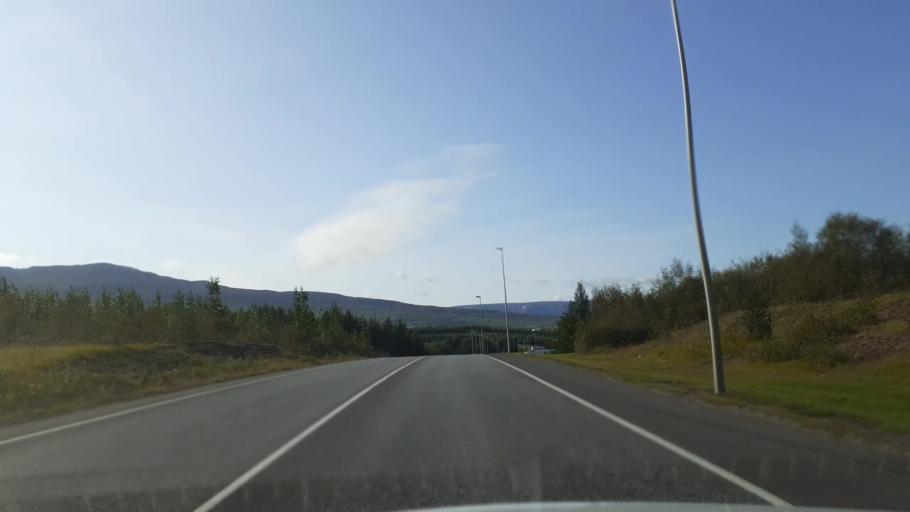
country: IS
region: Northeast
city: Akureyri
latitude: 65.6732
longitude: -18.1245
